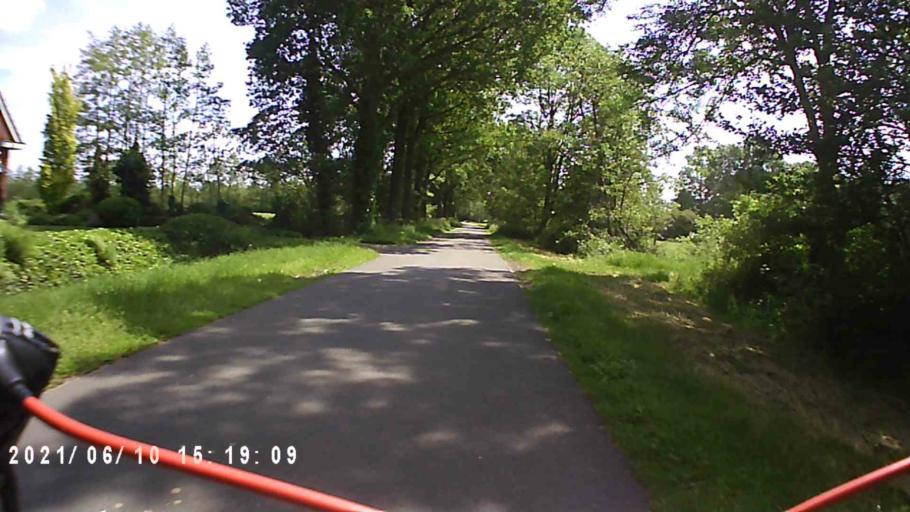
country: NL
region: Friesland
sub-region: Gemeente Achtkarspelen
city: Surhuisterveen
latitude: 53.1959
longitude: 6.1711
